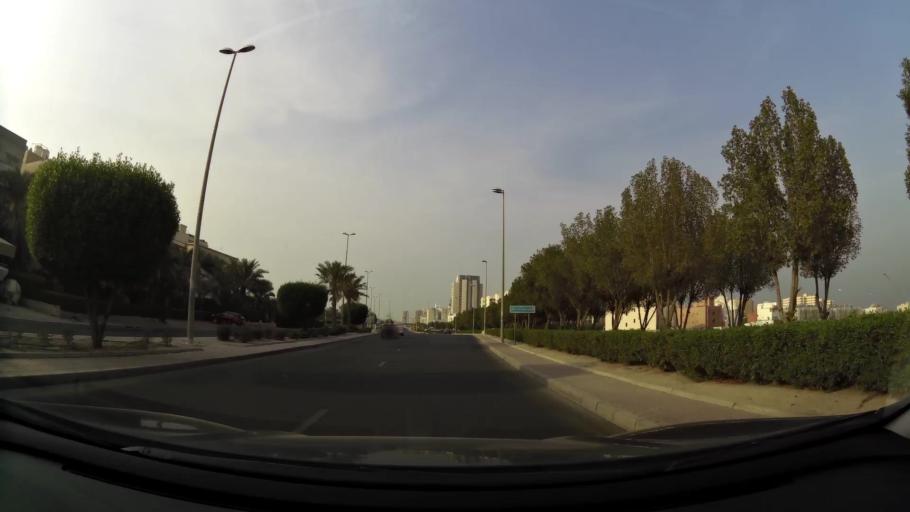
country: KW
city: Al Funaytis
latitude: 29.2437
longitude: 48.0827
